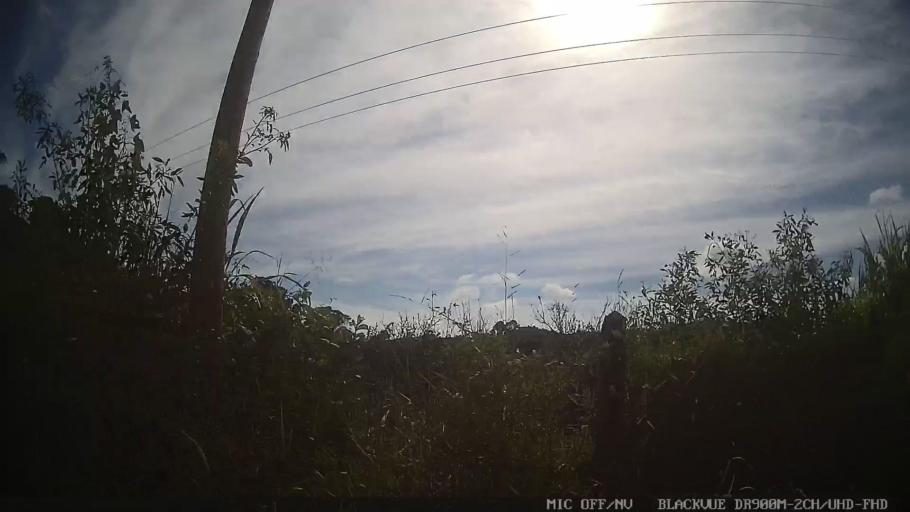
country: BR
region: Sao Paulo
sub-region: Braganca Paulista
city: Braganca Paulista
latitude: -23.0238
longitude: -46.6373
